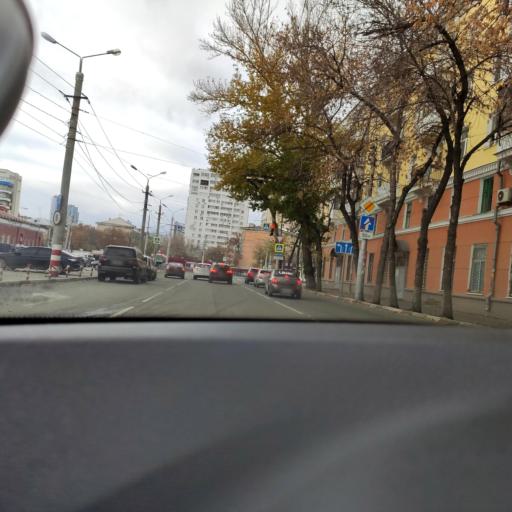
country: RU
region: Samara
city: Samara
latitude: 53.1952
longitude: 50.1263
